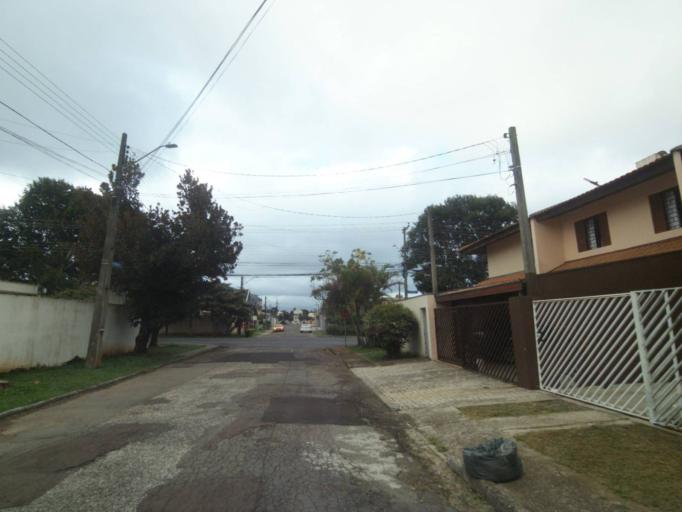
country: BR
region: Parana
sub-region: Pinhais
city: Pinhais
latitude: -25.4592
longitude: -49.2179
